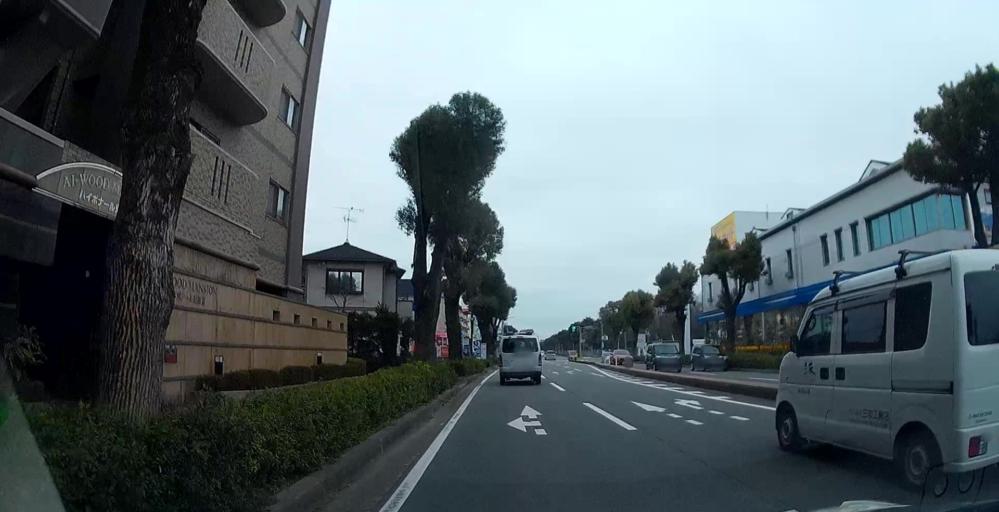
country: JP
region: Kumamoto
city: Kumamoto
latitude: 32.7893
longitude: 130.7719
